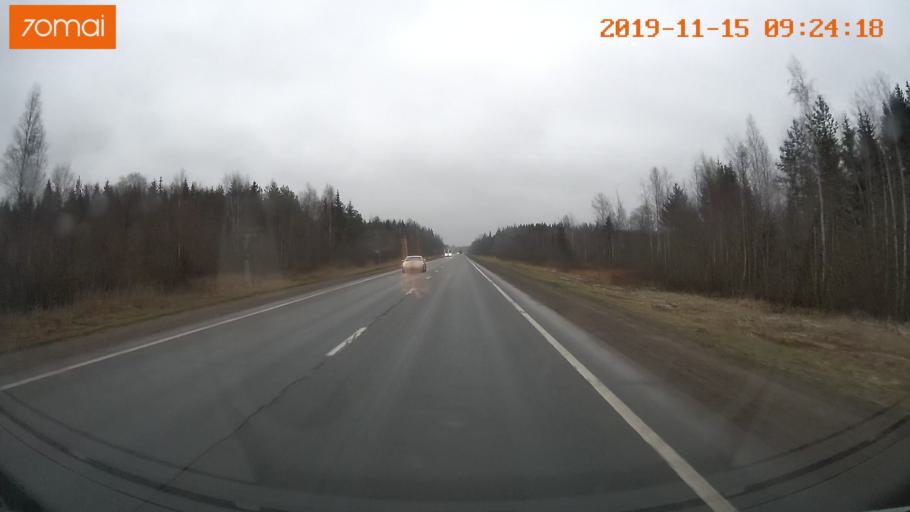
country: RU
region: Vologda
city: Tonshalovo
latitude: 59.3039
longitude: 38.1348
